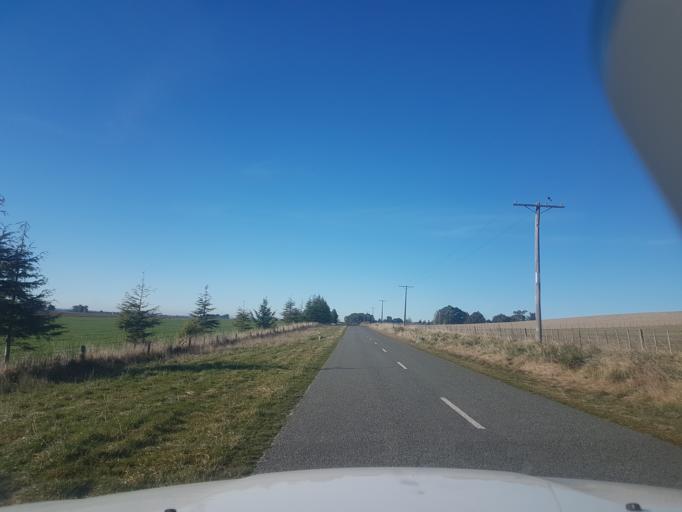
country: NZ
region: Canterbury
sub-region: Timaru District
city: Pleasant Point
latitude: -44.2892
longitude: 171.0733
